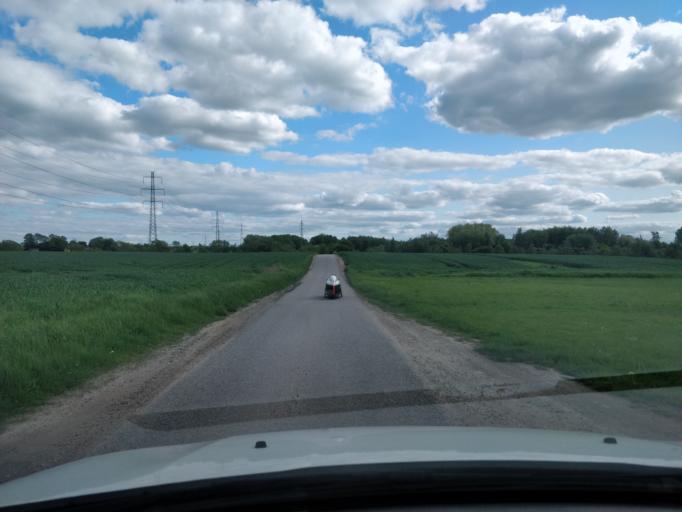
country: DK
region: Capital Region
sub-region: Hoje-Taastrup Kommune
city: Flong
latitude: 55.6838
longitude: 12.2193
